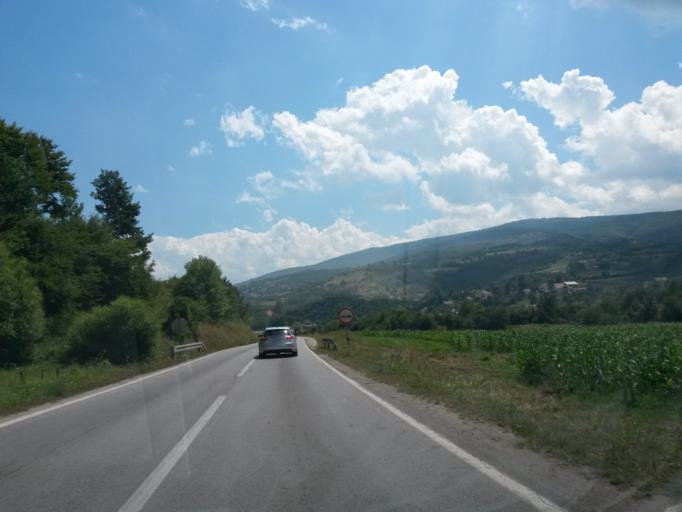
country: BA
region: Federation of Bosnia and Herzegovina
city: Turbe
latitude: 44.2386
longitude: 17.6064
